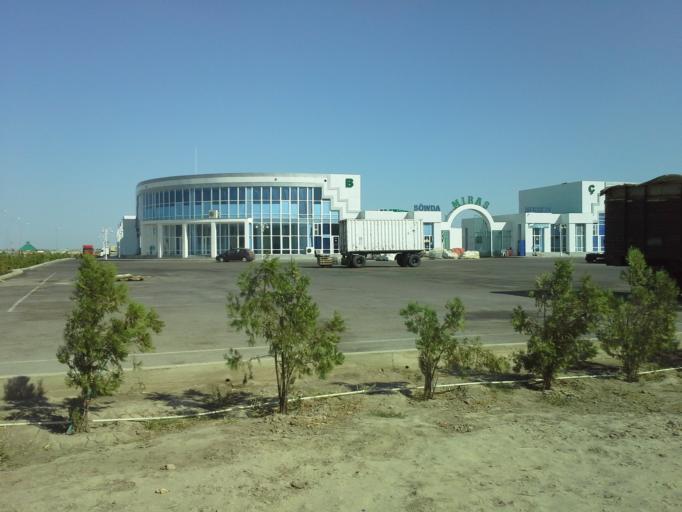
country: TM
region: Dasoguz
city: Dasoguz
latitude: 41.8092
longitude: 59.9540
